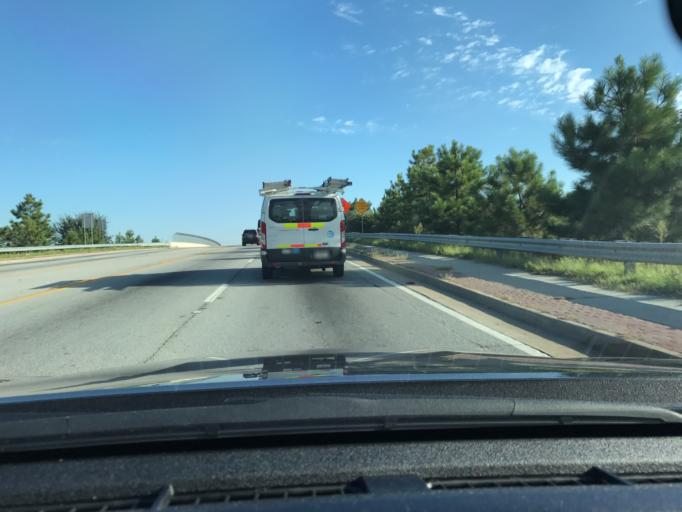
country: US
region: Georgia
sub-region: Clayton County
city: Forest Park
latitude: 33.6250
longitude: -84.3843
